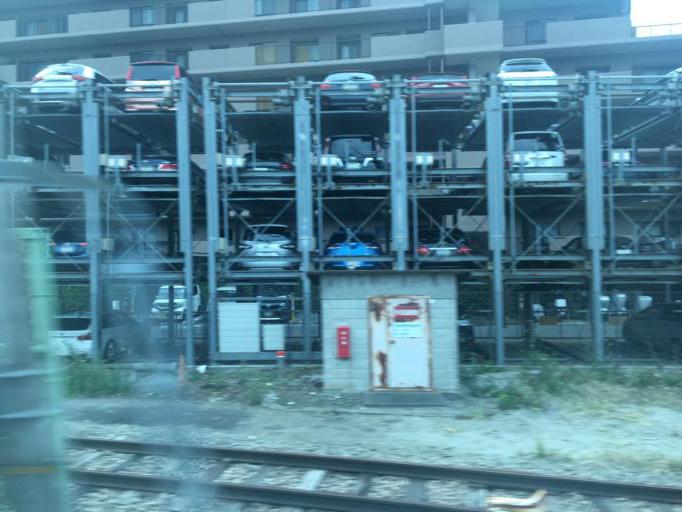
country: JP
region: Tokyo
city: Hino
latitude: 35.6944
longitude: 139.4236
